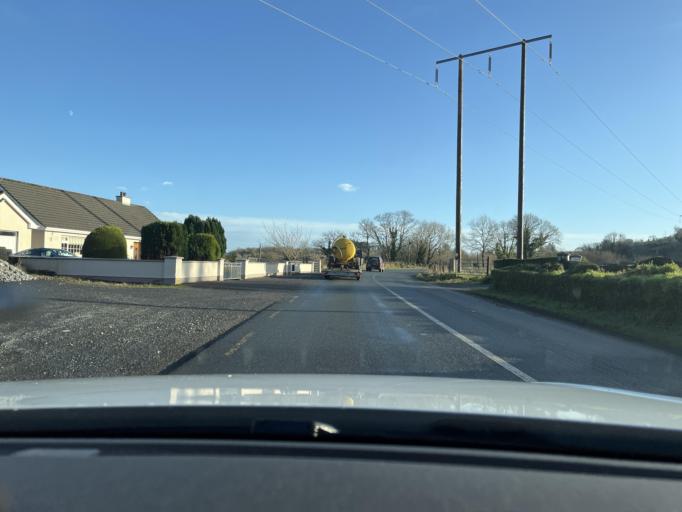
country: IE
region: Connaught
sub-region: County Leitrim
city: Manorhamilton
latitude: 54.1871
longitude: -8.1649
